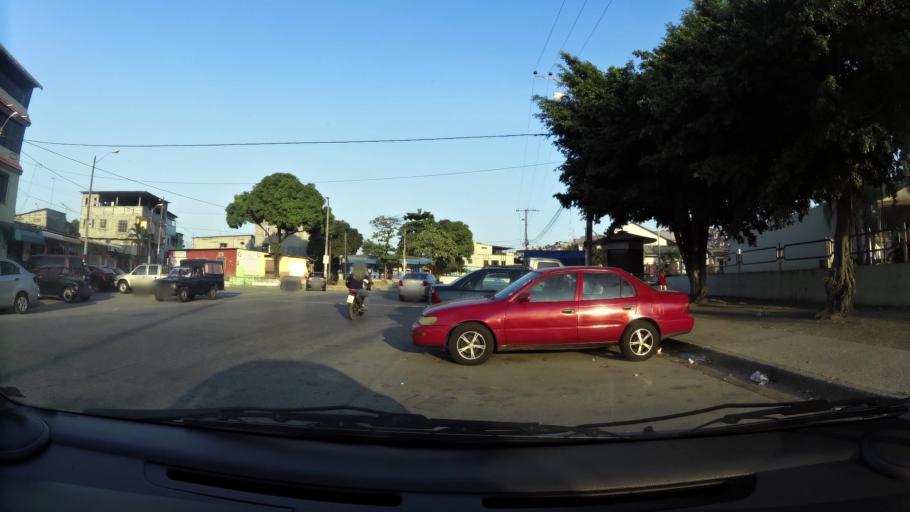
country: EC
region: Guayas
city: Guayaquil
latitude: -2.1447
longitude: -79.9232
